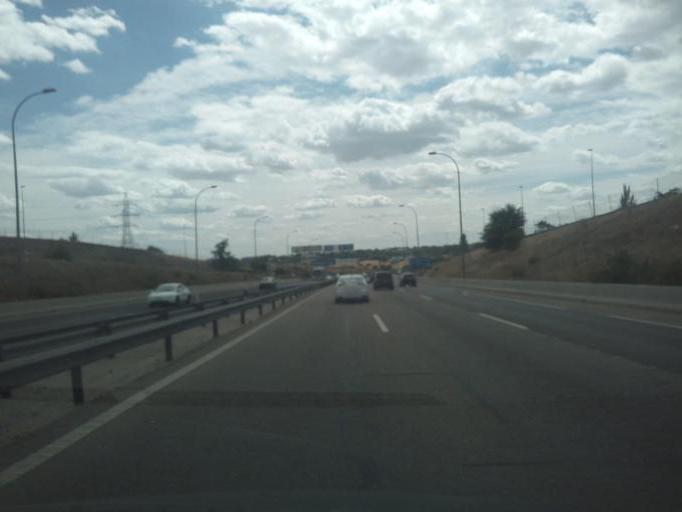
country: ES
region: Madrid
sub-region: Provincia de Madrid
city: San Sebastian de los Reyes
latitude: 40.5460
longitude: -3.6081
